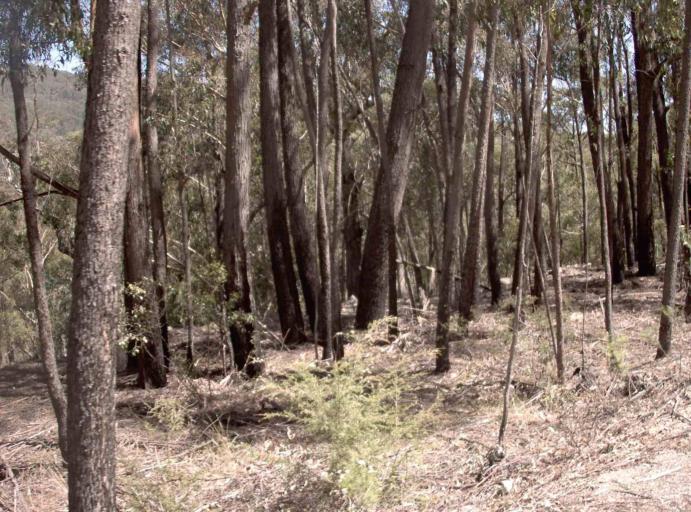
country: AU
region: Victoria
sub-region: East Gippsland
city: Lakes Entrance
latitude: -37.3771
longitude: 148.2166
